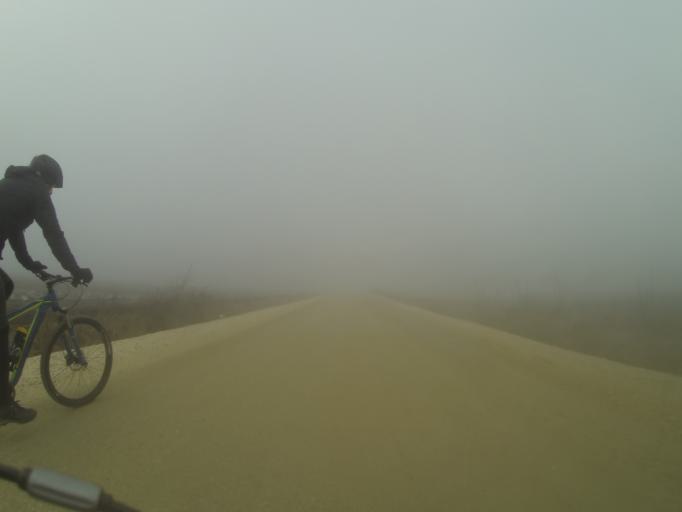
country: RO
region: Mehedinti
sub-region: Comuna Baclesu
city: Baclesu
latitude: 44.4497
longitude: 23.1255
